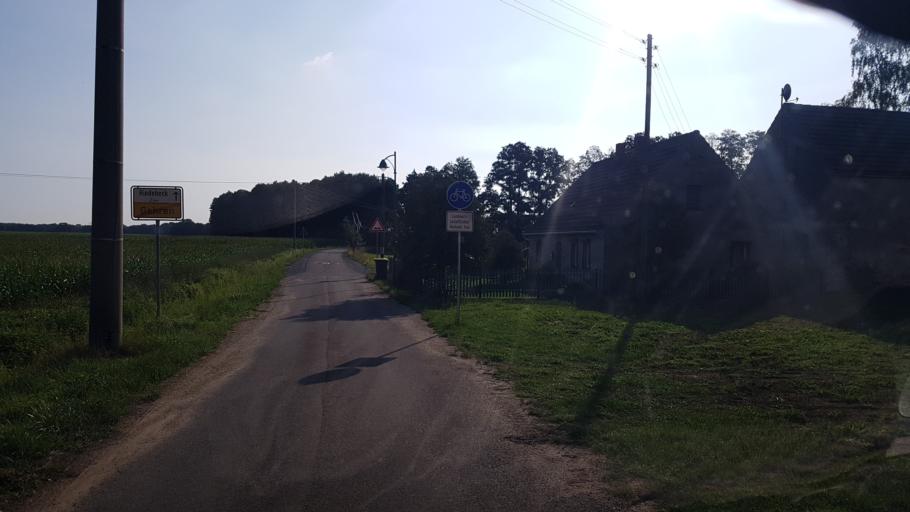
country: DE
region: Brandenburg
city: Luckau
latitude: 51.8031
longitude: 13.6535
